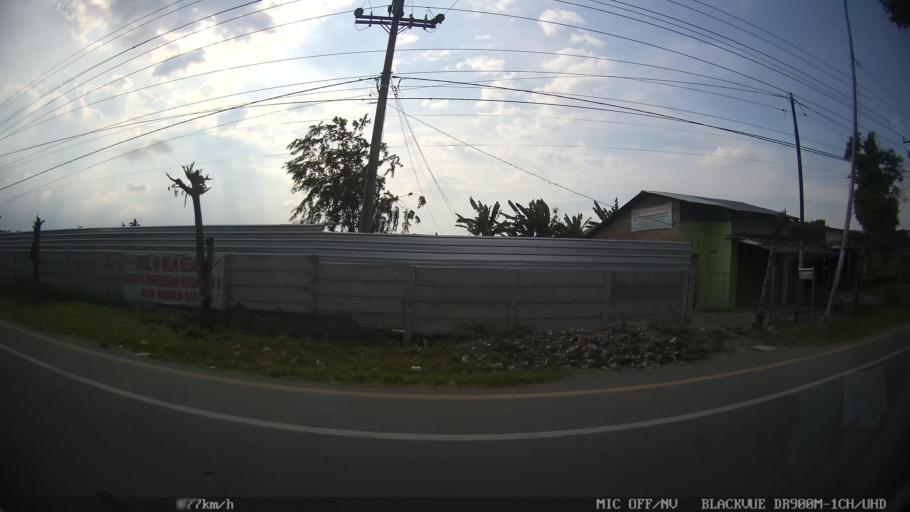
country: ID
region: North Sumatra
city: Percut
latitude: 3.5675
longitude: 98.7954
